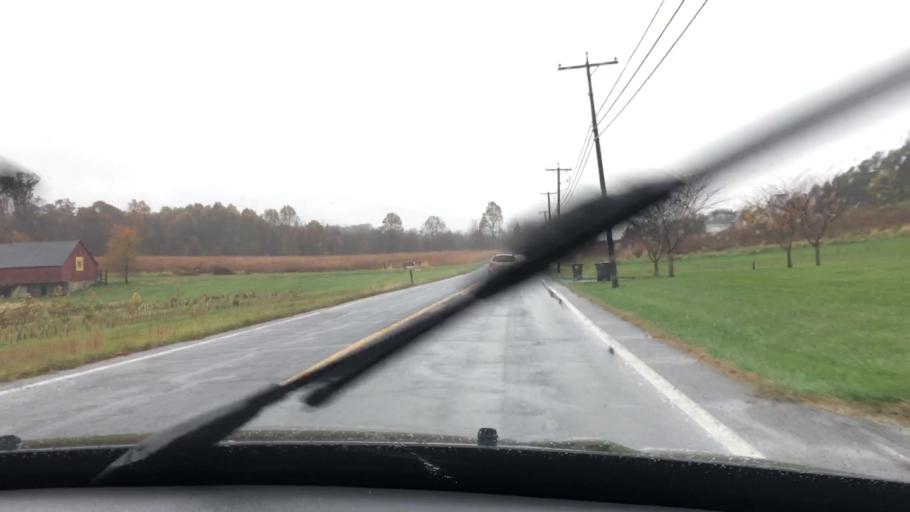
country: US
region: Maryland
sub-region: Carroll County
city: Manchester
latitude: 39.6865
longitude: -76.8815
